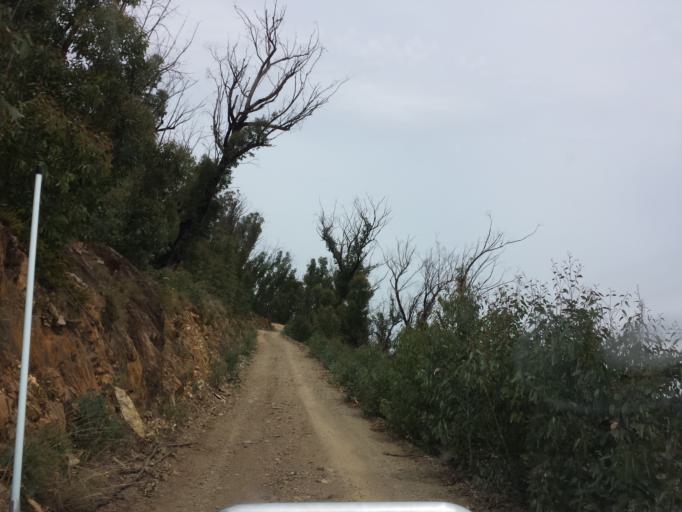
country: AU
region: Victoria
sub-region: Wellington
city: Heyfield
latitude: -37.7565
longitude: 146.5150
